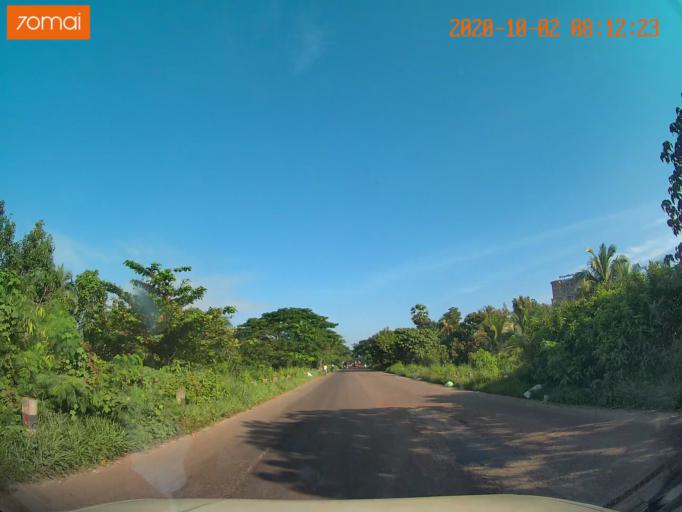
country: IN
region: Kerala
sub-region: Kozhikode
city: Kozhikode
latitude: 11.2809
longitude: 75.8039
